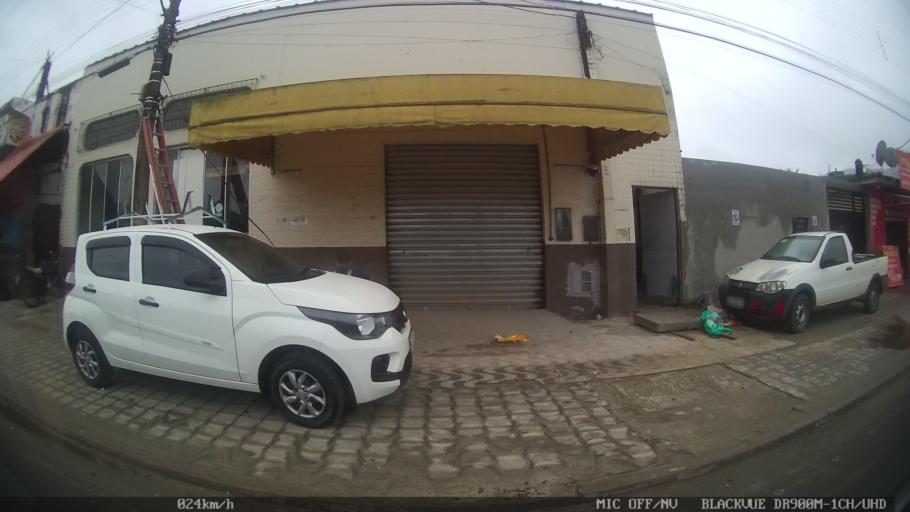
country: BR
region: Sao Paulo
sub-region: Juquia
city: Juquia
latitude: -24.3191
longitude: -47.6356
